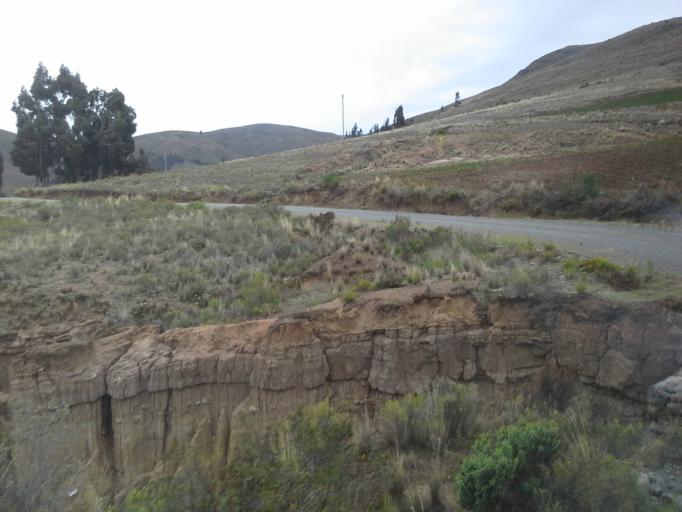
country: BO
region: Cochabamba
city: Colomi
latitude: -17.4043
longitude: -65.8131
